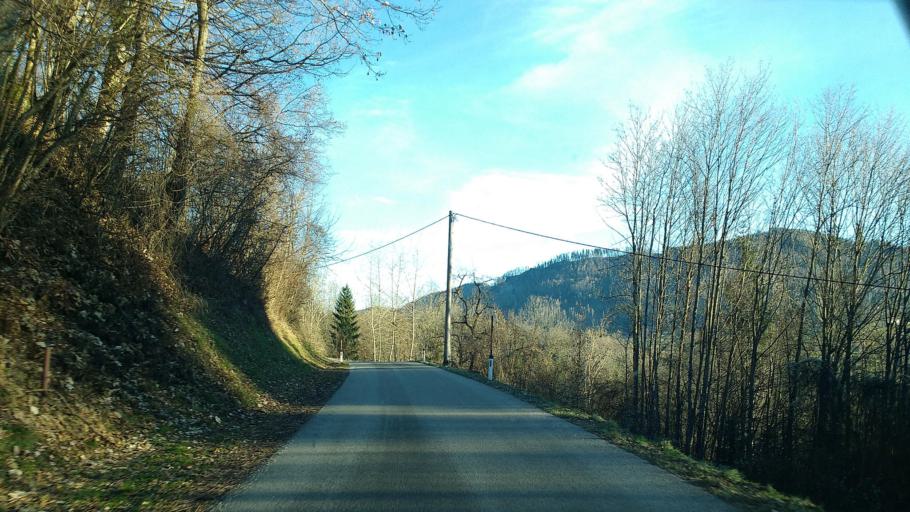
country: AT
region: Upper Austria
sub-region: Politischer Bezirk Kirchdorf an der Krems
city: Micheldorf in Oberoesterreich
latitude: 47.9049
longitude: 14.1491
